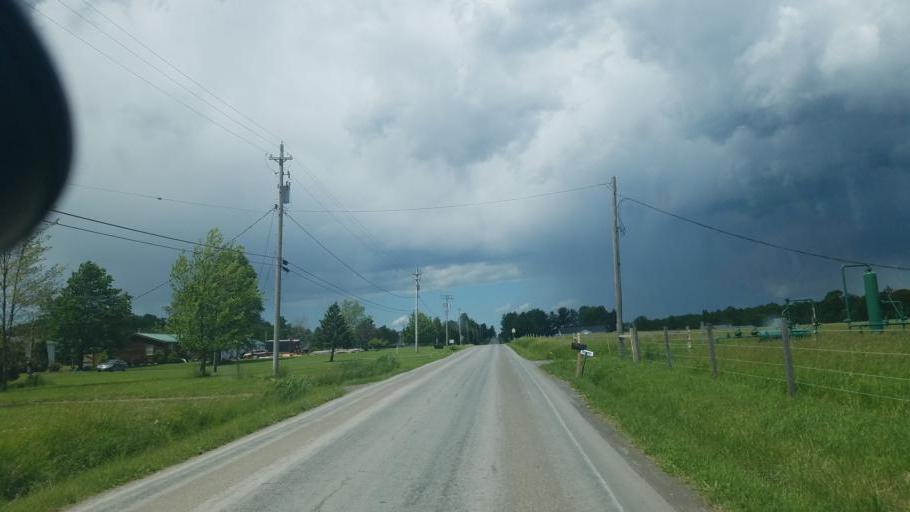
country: US
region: Ohio
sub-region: Geauga County
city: Middlefield
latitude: 41.4601
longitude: -81.0033
